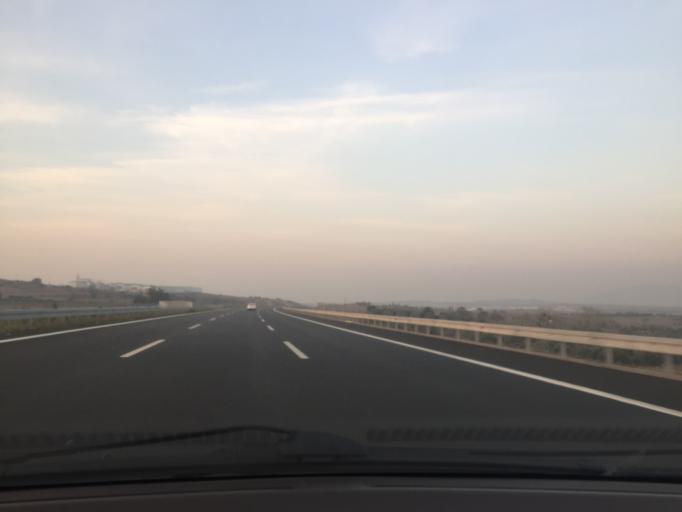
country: TR
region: Bursa
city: Karacabey
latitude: 40.2595
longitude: 28.4809
